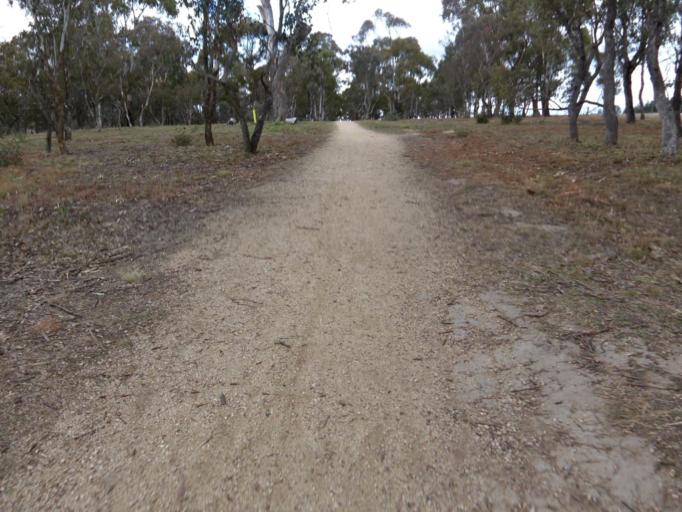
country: AU
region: Australian Capital Territory
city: Macquarie
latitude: -35.2845
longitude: 149.0812
